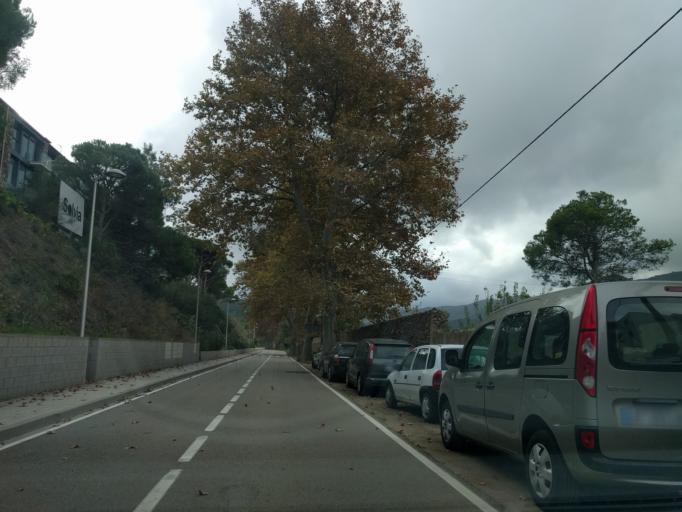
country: ES
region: Catalonia
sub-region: Provincia de Girona
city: Llanca
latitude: 42.3343
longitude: 3.2041
